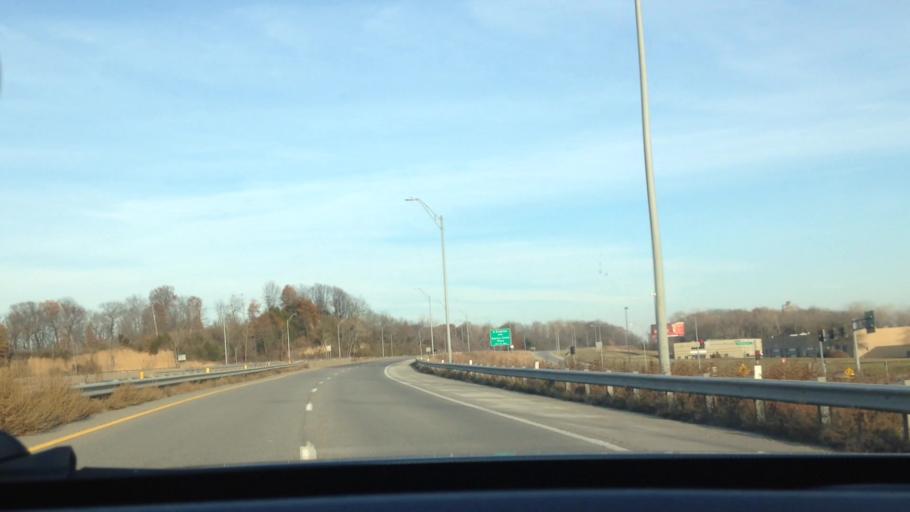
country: US
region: Missouri
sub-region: Clay County
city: North Kansas City
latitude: 39.1500
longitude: -94.5368
